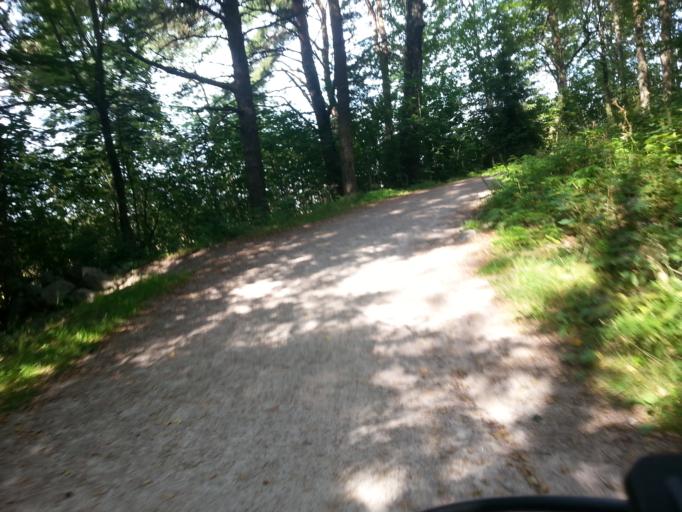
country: FI
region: Uusimaa
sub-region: Helsinki
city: Vantaa
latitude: 60.2201
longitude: 25.0049
